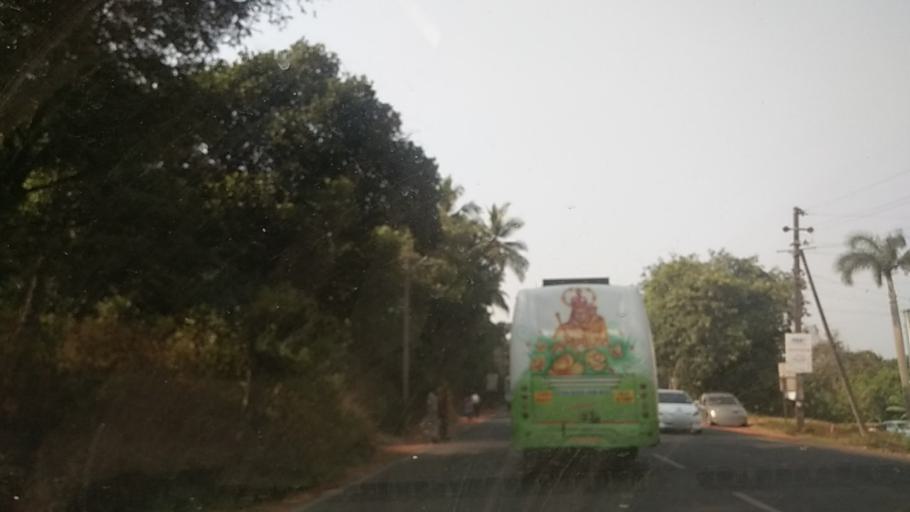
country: IN
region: Goa
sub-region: North Goa
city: Serula
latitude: 15.5453
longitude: 73.8198
